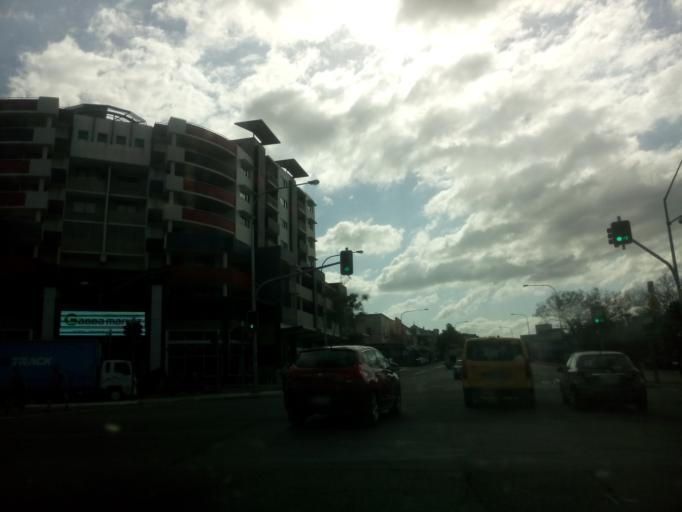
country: AU
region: Queensland
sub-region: Brisbane
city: Woolloongabba
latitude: -27.4865
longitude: 153.0361
